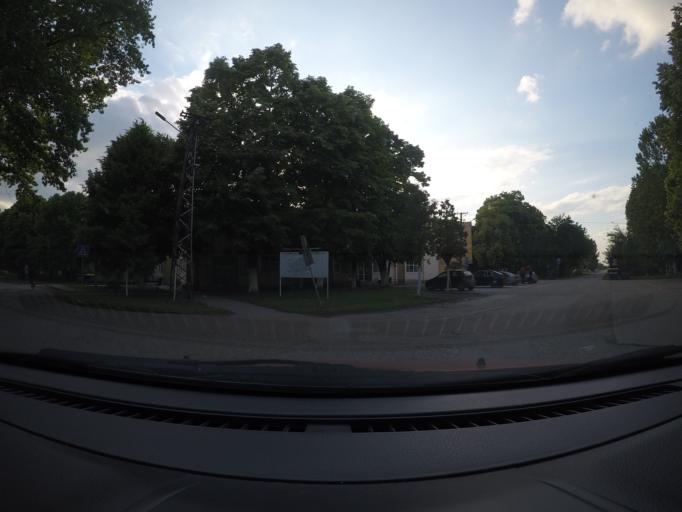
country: RS
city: Debeljaca
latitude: 45.0692
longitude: 20.5991
